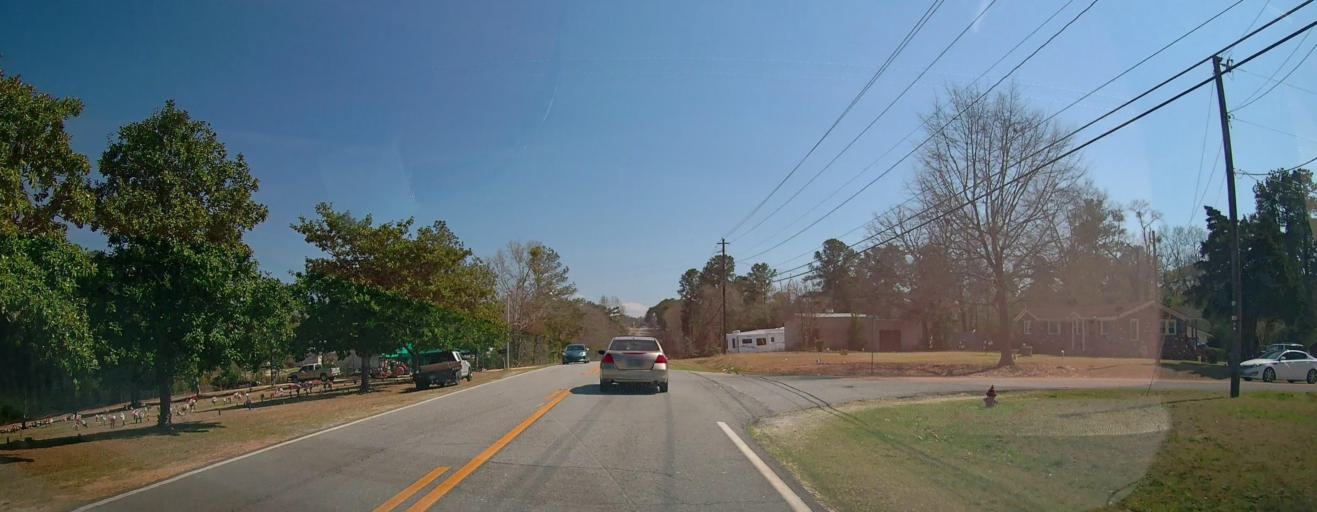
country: US
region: Georgia
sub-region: Bibb County
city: Macon
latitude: 32.8786
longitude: -83.5668
